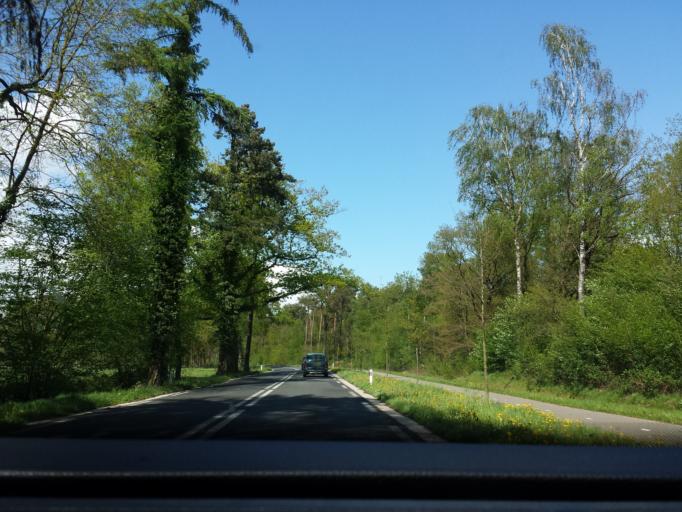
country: NL
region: Gelderland
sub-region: Gemeente Lochem
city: Barchem
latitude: 52.0611
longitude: 6.4276
